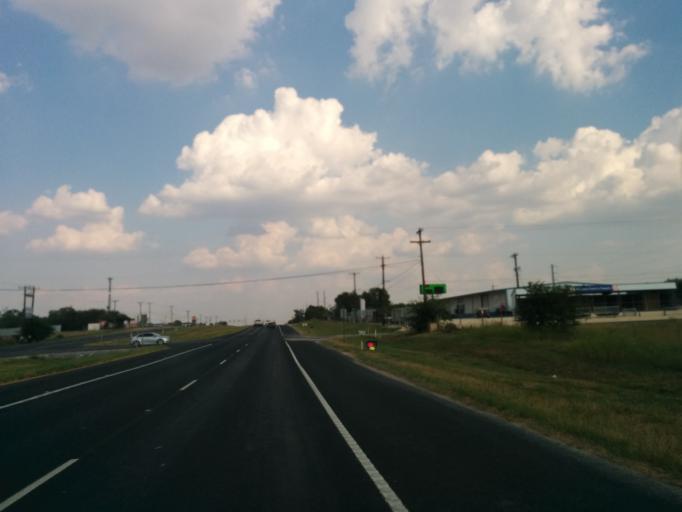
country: US
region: Texas
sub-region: Bexar County
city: Elmendorf
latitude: 29.2840
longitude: -98.3418
